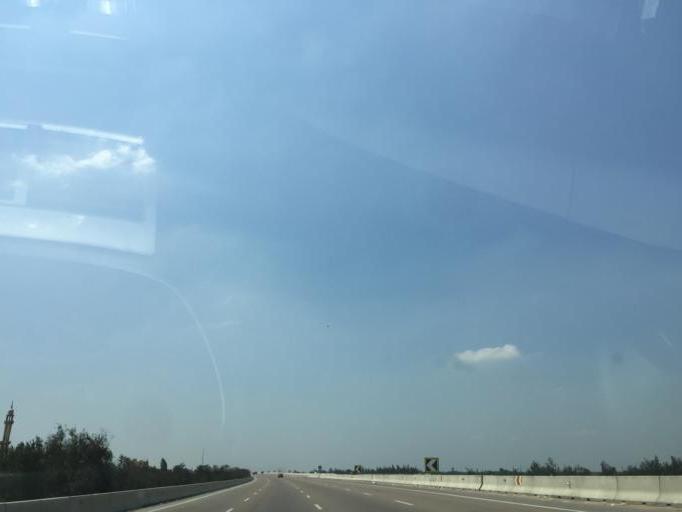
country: EG
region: Al Buhayrah
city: Beheira
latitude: 30.5334
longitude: 30.2235
